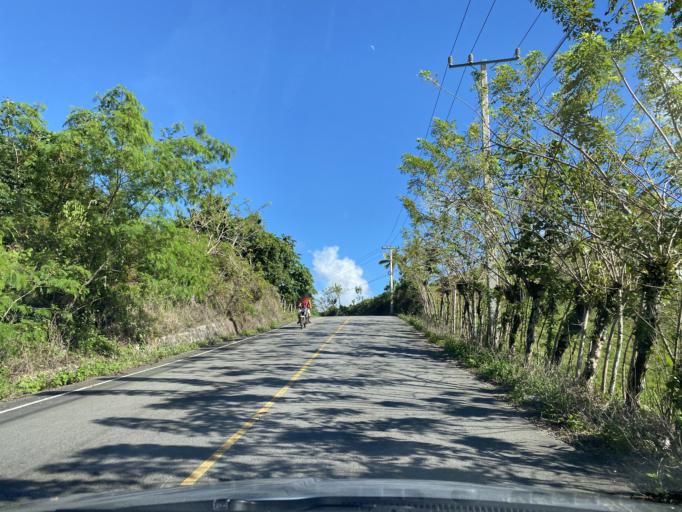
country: DO
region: Samana
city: Sanchez
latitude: 19.2504
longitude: -69.5905
